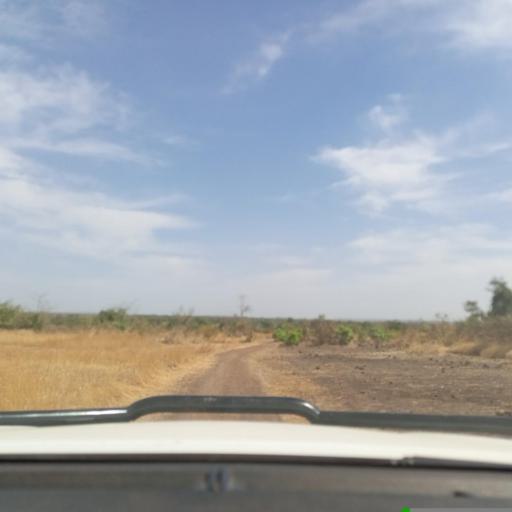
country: ML
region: Koulikoro
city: Kati
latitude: 12.7491
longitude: -8.2432
